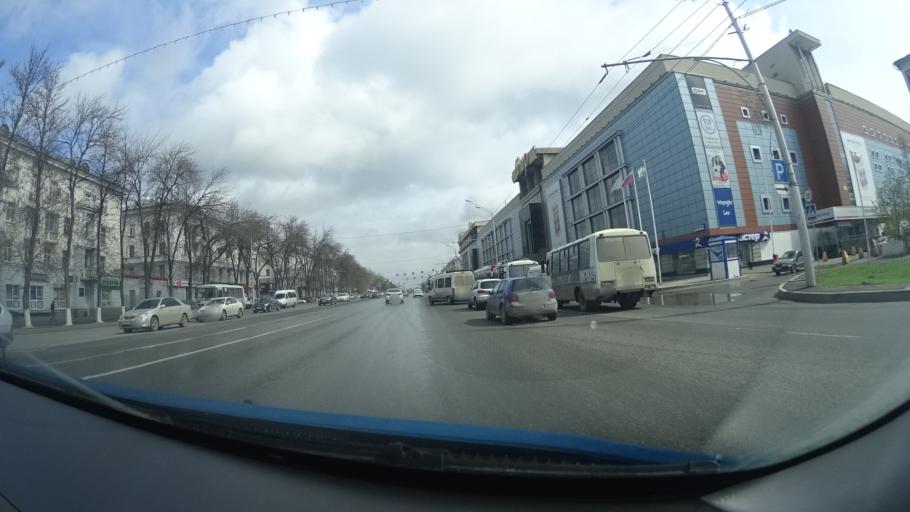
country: RU
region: Bashkortostan
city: Ufa
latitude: 54.7406
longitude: 55.9830
